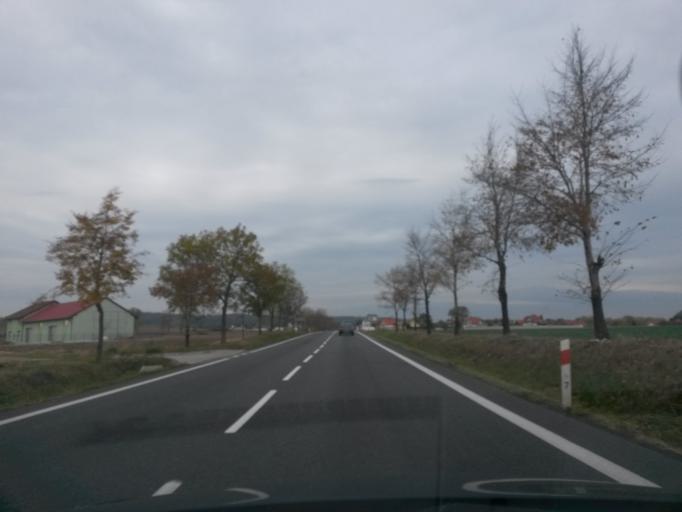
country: PL
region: Lower Silesian Voivodeship
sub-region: Powiat dzierzoniowski
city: Niemcza
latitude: 50.6792
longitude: 16.8242
